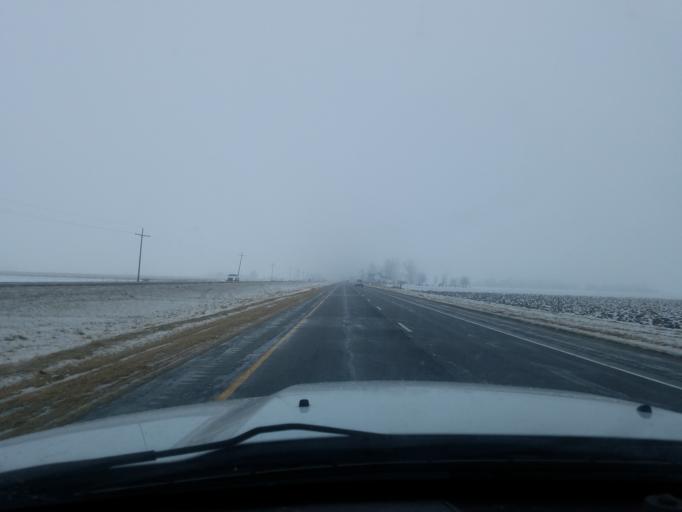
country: US
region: Indiana
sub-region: Howard County
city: Indian Heights
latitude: 40.3378
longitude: -86.1270
